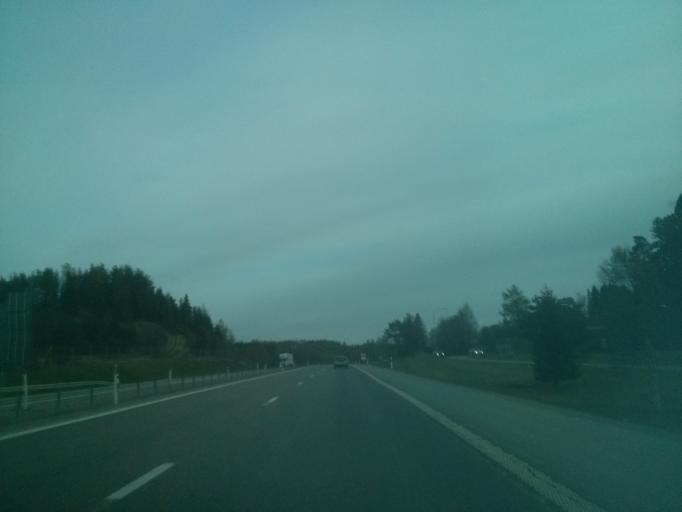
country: SE
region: Vaesternorrland
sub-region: Sundsvalls Kommun
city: Sundsbruk
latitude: 62.4322
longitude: 17.3434
